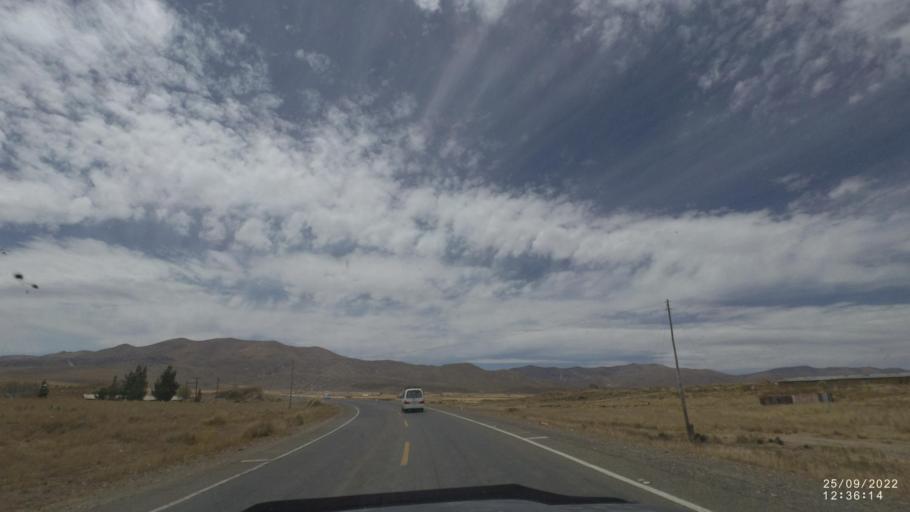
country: BO
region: Oruro
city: Machacamarca
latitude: -18.1665
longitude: -66.9903
